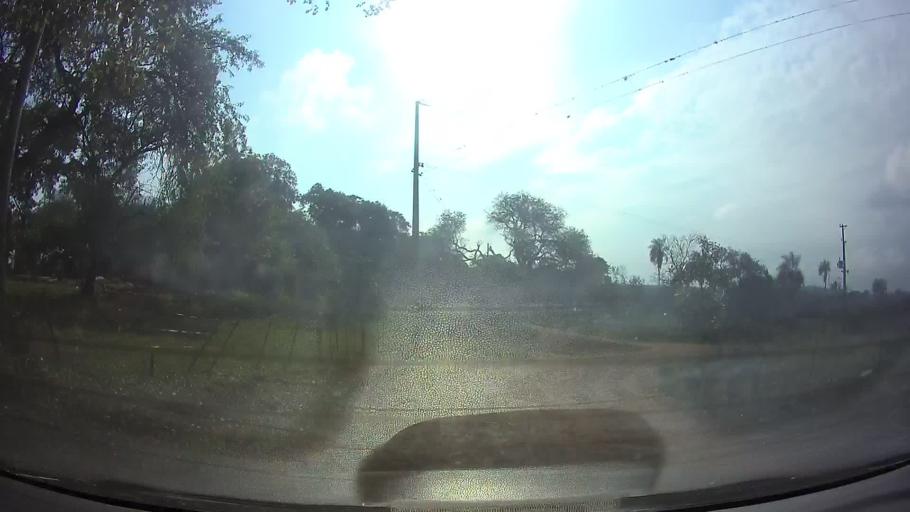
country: PY
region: Cordillera
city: Arroyos y Esteros
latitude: -25.0092
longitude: -57.1994
